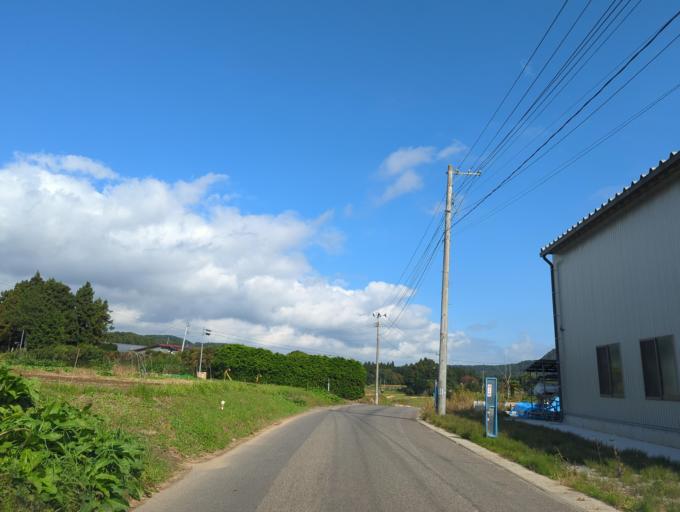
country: JP
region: Fukushima
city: Motomiya
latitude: 37.5538
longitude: 140.3446
